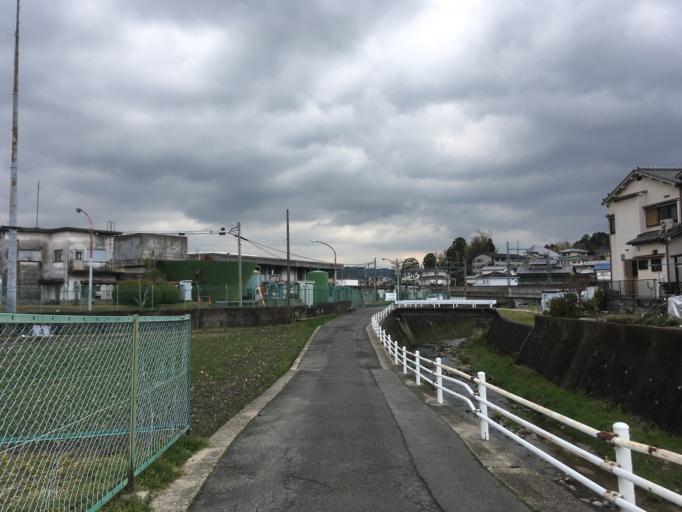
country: JP
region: Nara
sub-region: Ikoma-shi
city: Ikoma
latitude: 34.6896
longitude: 135.7047
